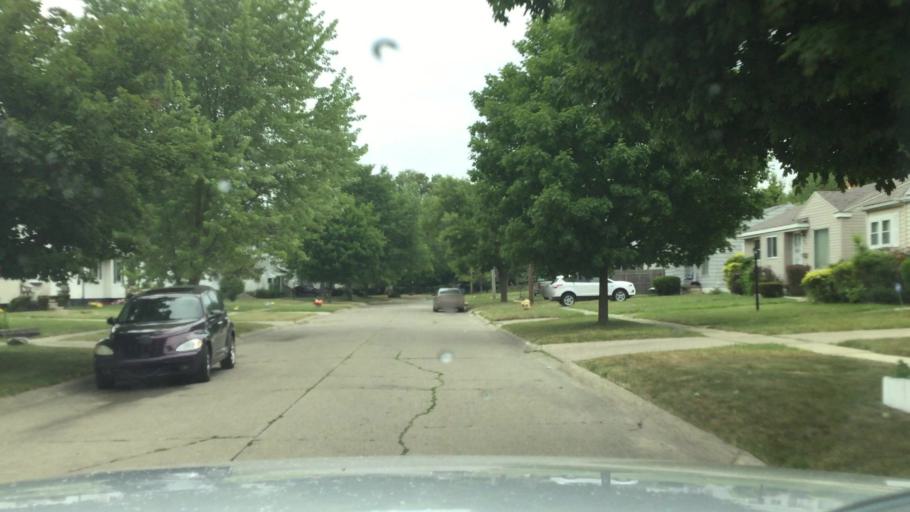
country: US
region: Michigan
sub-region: Genesee County
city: Beecher
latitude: 43.0549
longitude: -83.7246
